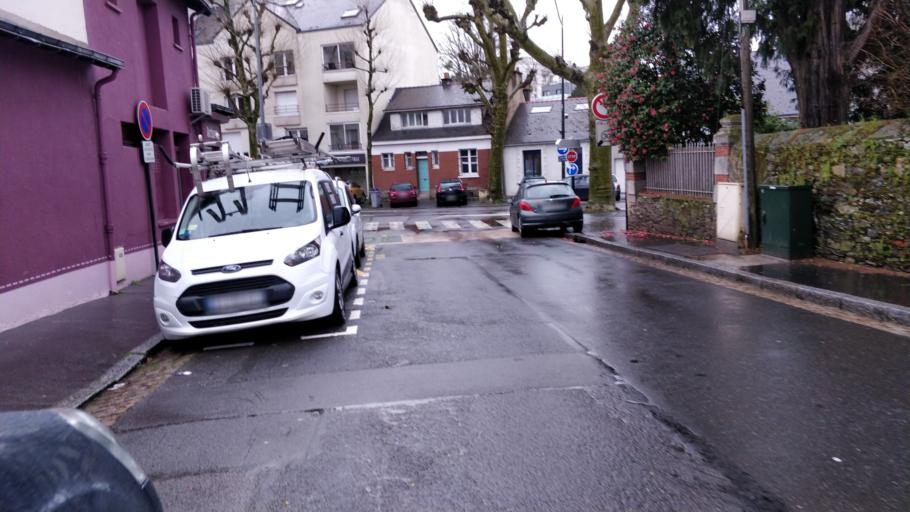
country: FR
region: Pays de la Loire
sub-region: Departement de la Loire-Atlantique
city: Nantes
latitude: 47.2350
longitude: -1.5457
